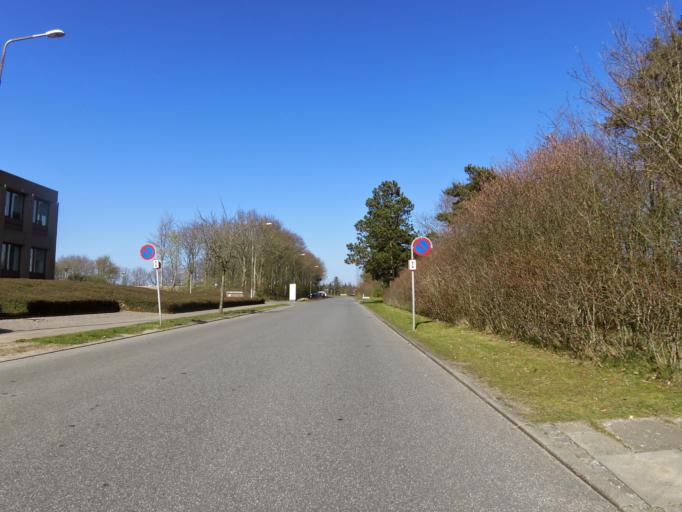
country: DK
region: South Denmark
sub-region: Esbjerg Kommune
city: Ribe
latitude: 55.3521
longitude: 8.7881
